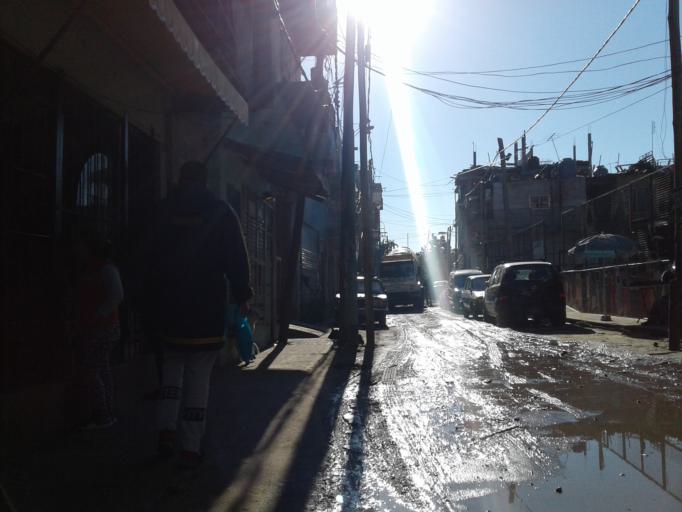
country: AR
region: Buenos Aires F.D.
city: Villa Lugano
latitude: -34.6725
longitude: -58.4626
